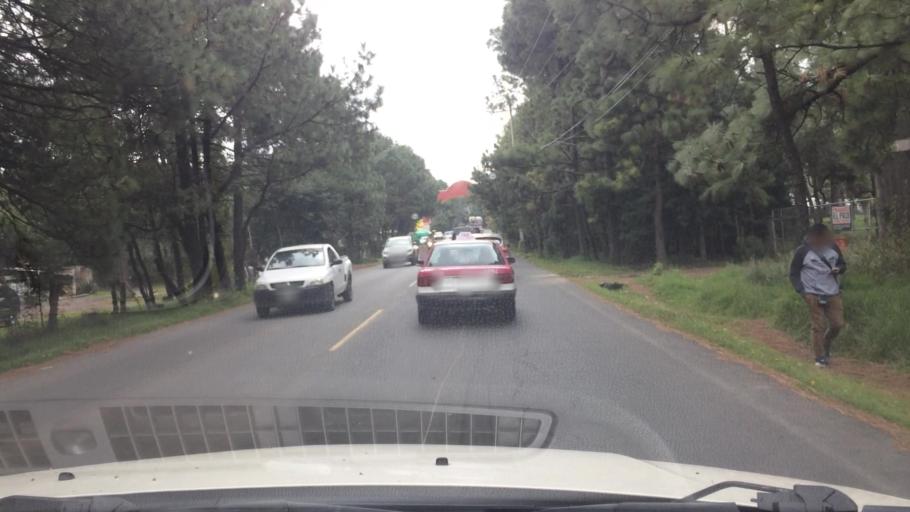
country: MX
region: Mexico City
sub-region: Tlalpan
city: Lomas de Tepemecatl
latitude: 19.2474
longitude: -99.2423
